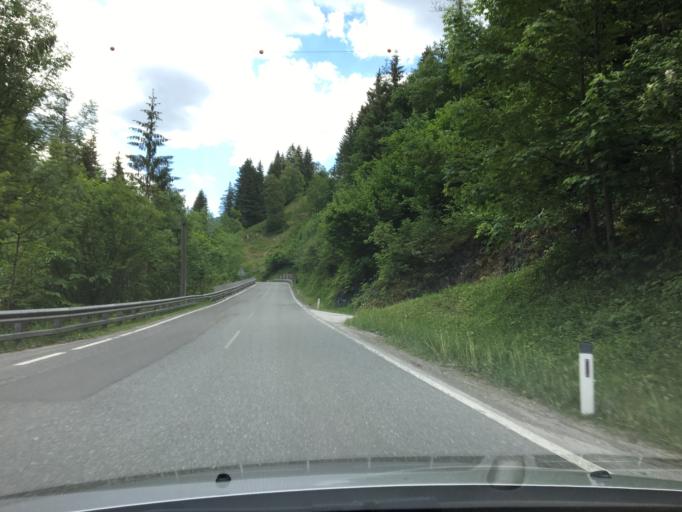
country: AT
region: Salzburg
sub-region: Politischer Bezirk Sankt Johann im Pongau
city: Wagrain
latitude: 47.3358
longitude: 13.2689
